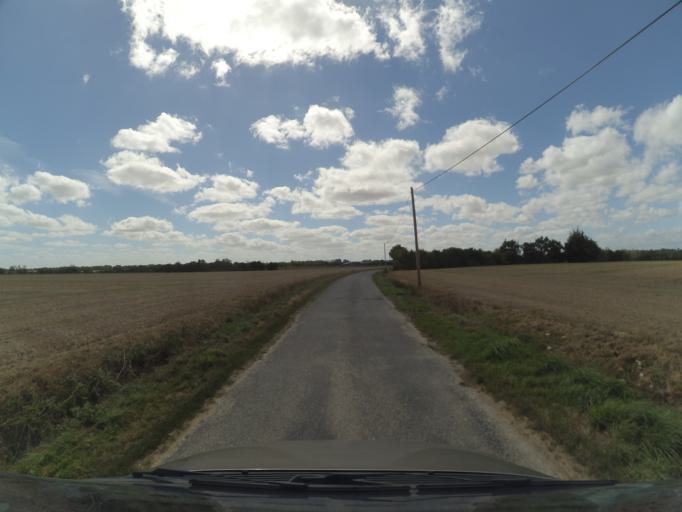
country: FR
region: Pays de la Loire
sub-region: Departement de la Loire-Atlantique
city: Saint-Hilaire-de-Clisson
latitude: 47.0493
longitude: -1.3364
